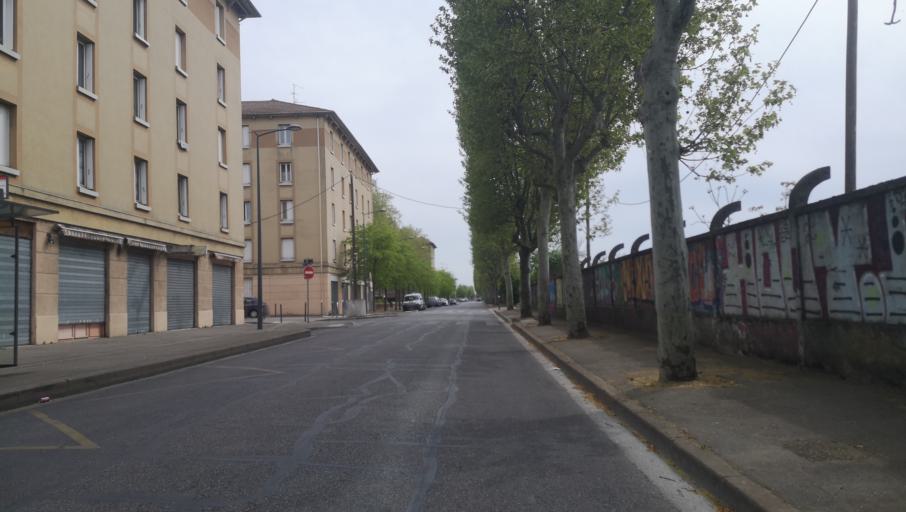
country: FR
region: Rhone-Alpes
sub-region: Departement du Rhone
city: Vaulx-en-Velin
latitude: 45.7614
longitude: 4.9291
